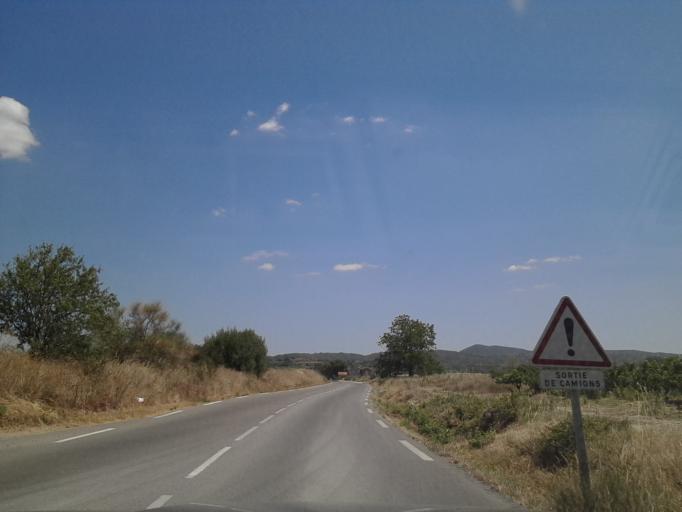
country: FR
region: Languedoc-Roussillon
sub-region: Departement de l'Herault
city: Saint-Jean-de-Fos
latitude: 43.7014
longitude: 3.5682
